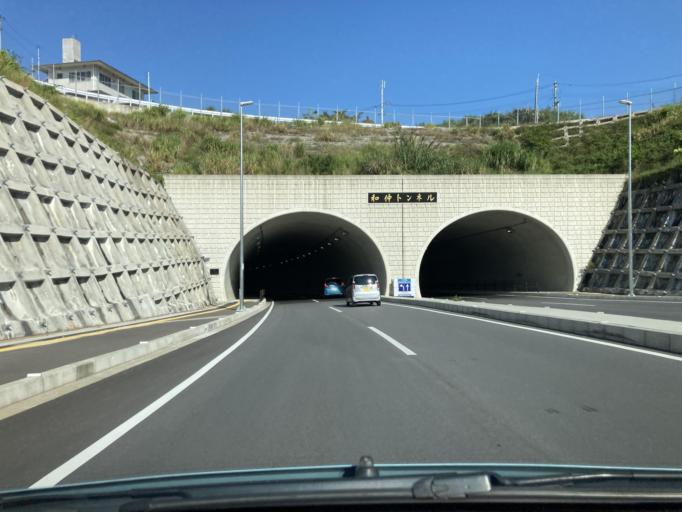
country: JP
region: Okinawa
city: Chatan
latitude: 26.2985
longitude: 127.8005
